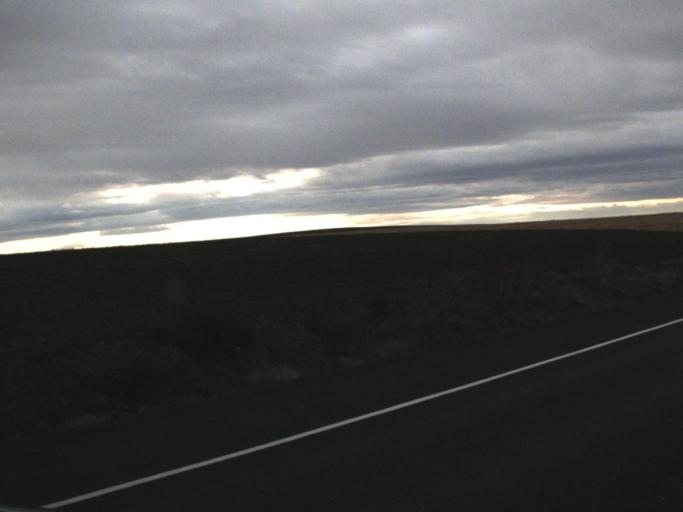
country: US
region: Washington
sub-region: Adams County
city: Ritzville
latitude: 46.7952
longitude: -118.4207
